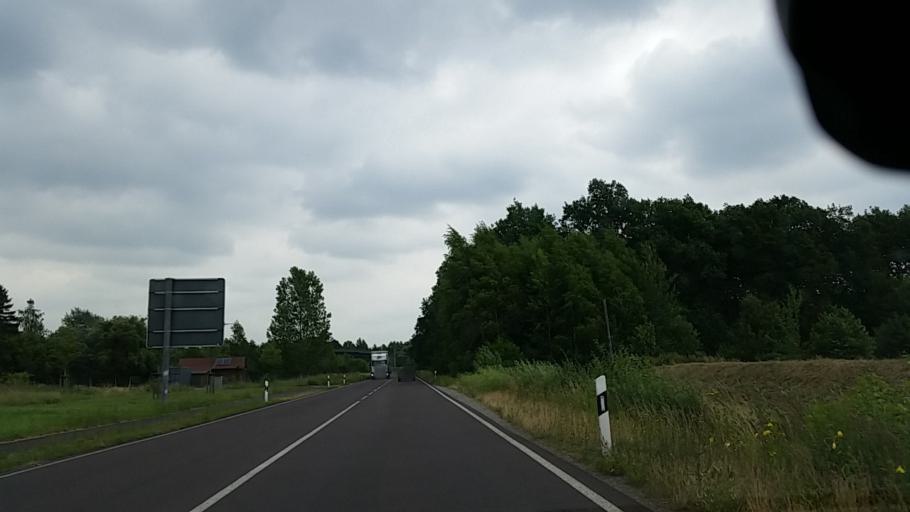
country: DE
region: Lower Saxony
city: Danndorf
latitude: 52.4322
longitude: 10.8652
